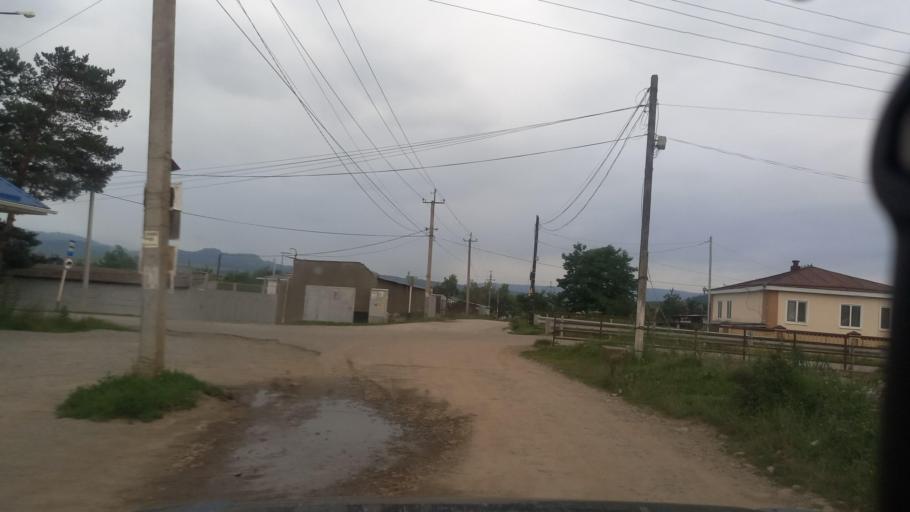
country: RU
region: Karachayevo-Cherkesiya
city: Pregradnaya
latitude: 43.9479
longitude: 41.1866
